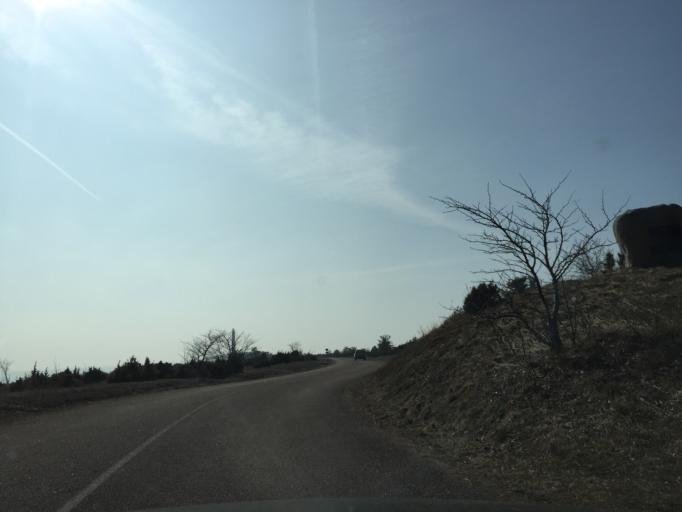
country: LV
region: Dundaga
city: Dundaga
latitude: 57.9177
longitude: 22.0639
